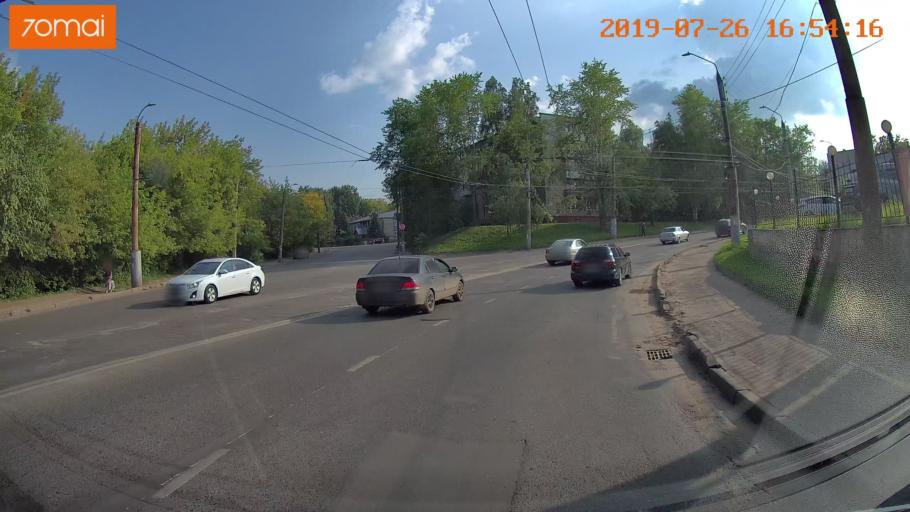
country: RU
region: Ivanovo
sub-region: Gorod Ivanovo
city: Ivanovo
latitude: 57.0114
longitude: 41.0006
